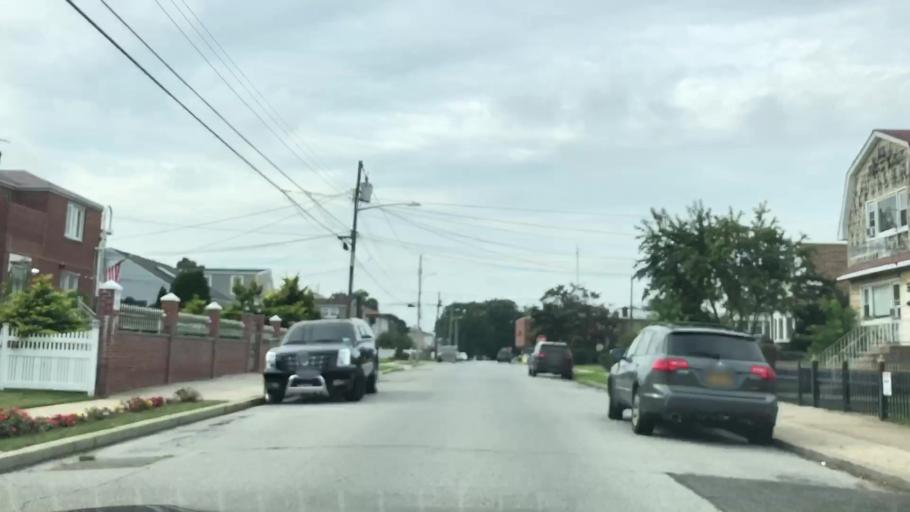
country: US
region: New York
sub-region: Nassau County
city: South Floral Park
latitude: 40.7037
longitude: -73.6940
